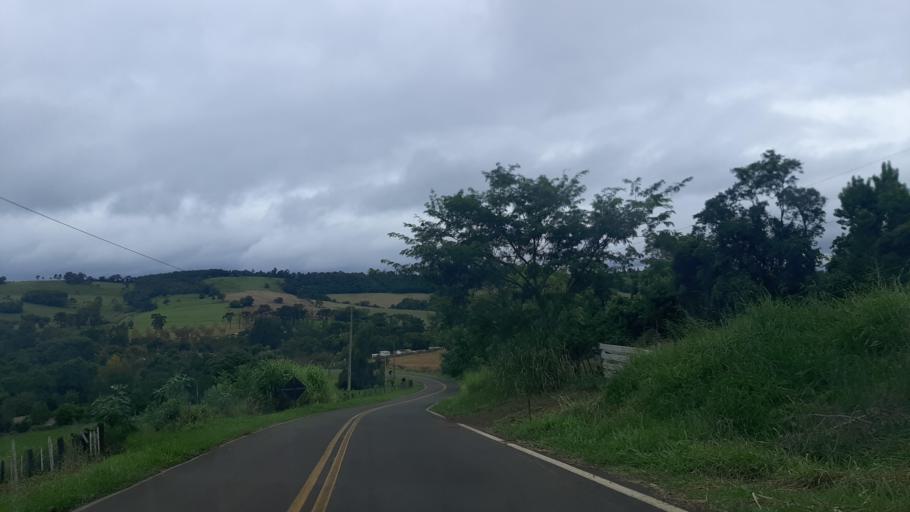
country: BR
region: Parana
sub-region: Ampere
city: Ampere
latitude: -25.9721
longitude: -53.4430
